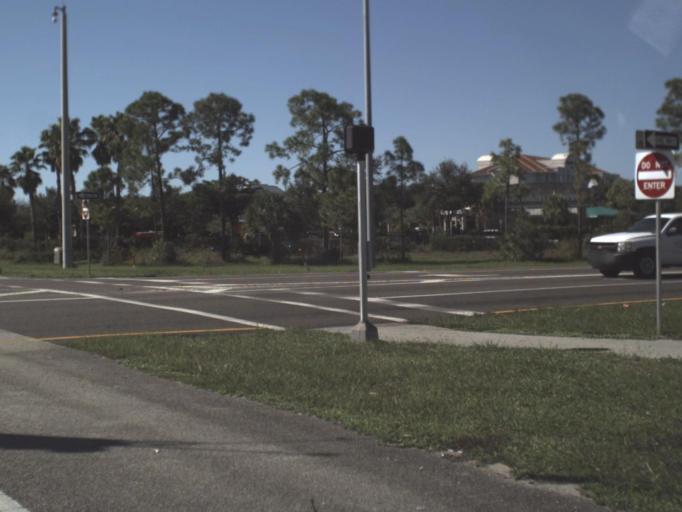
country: US
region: Florida
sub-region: Lee County
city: Gateway
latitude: 26.5474
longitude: -81.7963
